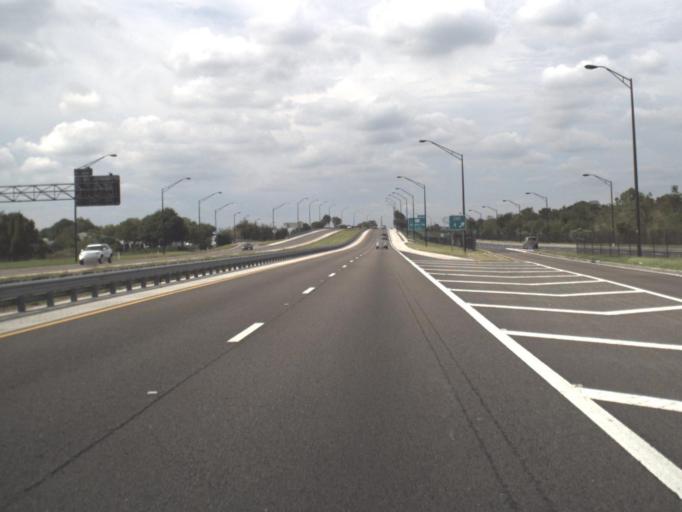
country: US
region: Florida
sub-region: Polk County
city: Medulla
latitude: 27.9981
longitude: -81.9925
